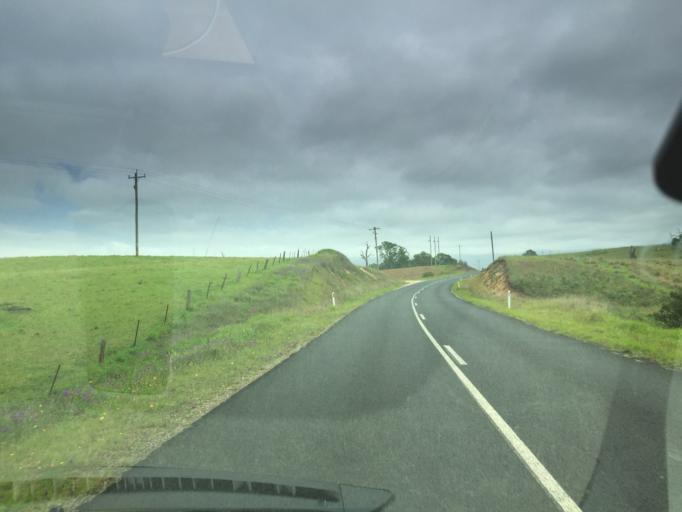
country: AU
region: New South Wales
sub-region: Bega Valley
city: Bega
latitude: -36.6558
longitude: 149.5829
